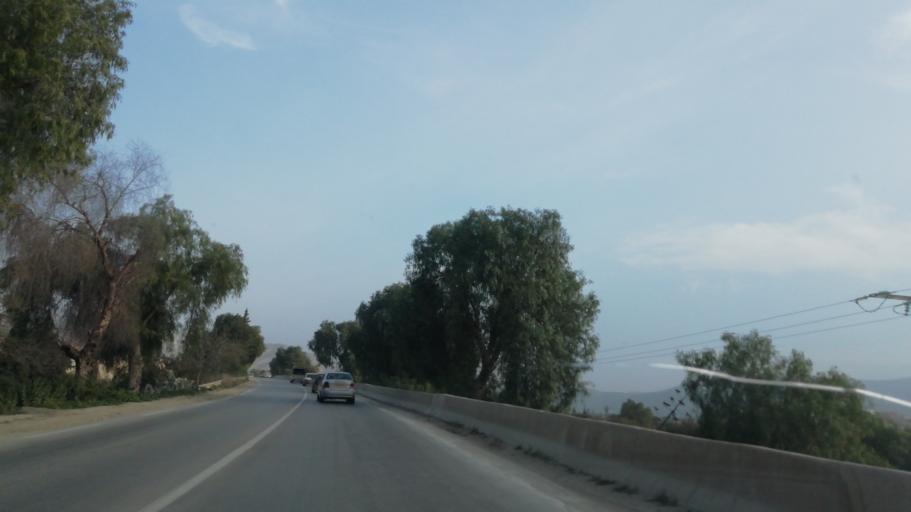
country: DZ
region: Mascara
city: Bou Hanifia el Hamamat
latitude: 35.4671
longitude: -0.0072
